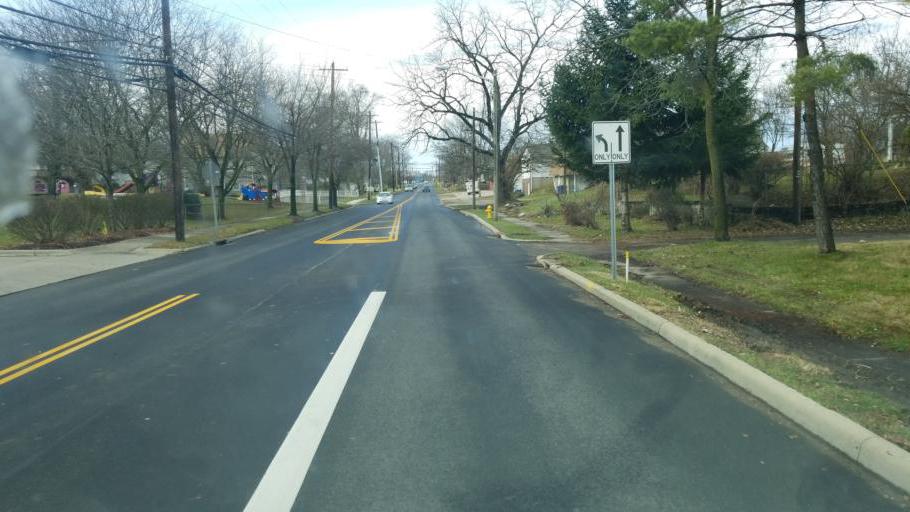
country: US
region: Ohio
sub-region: Delaware County
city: Delaware
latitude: 40.2906
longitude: -83.0748
